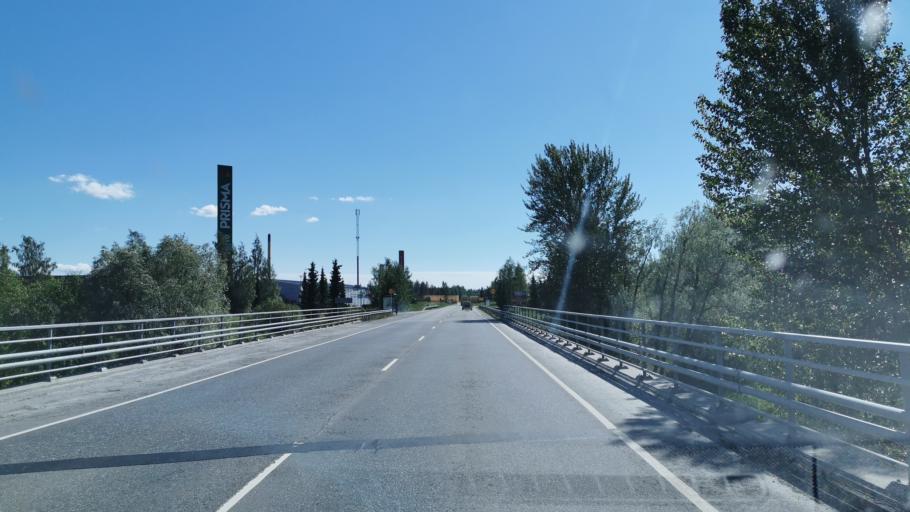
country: FI
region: Varsinais-Suomi
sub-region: Loimaa
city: Loimaa
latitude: 60.8589
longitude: 23.0449
